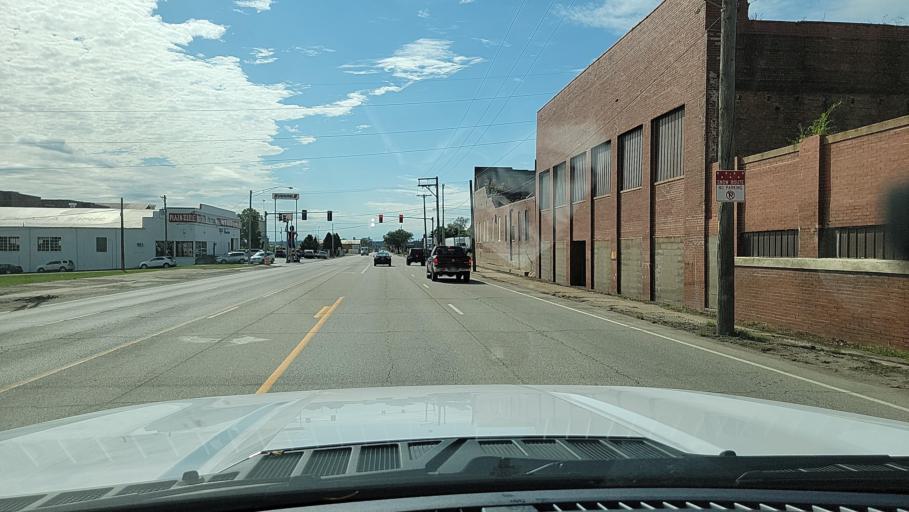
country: US
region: Illinois
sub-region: Peoria County
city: Peoria
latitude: 40.6789
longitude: -89.6071
